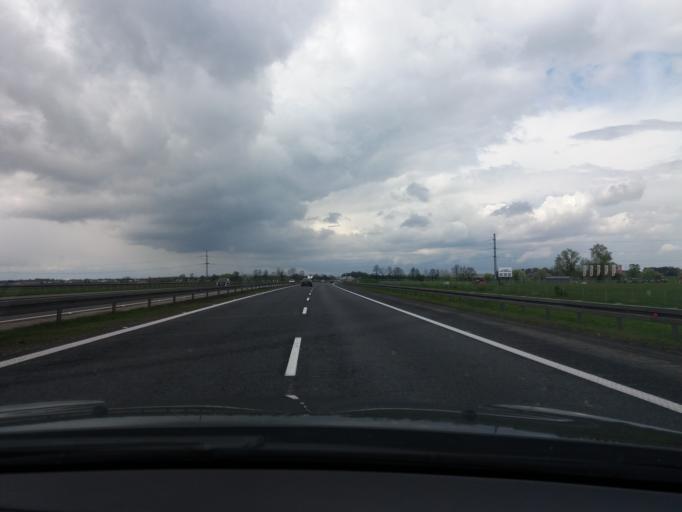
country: PL
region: Lower Silesian Voivodeship
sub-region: Powiat wroclawski
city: Zorawina
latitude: 51.0068
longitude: 17.0318
